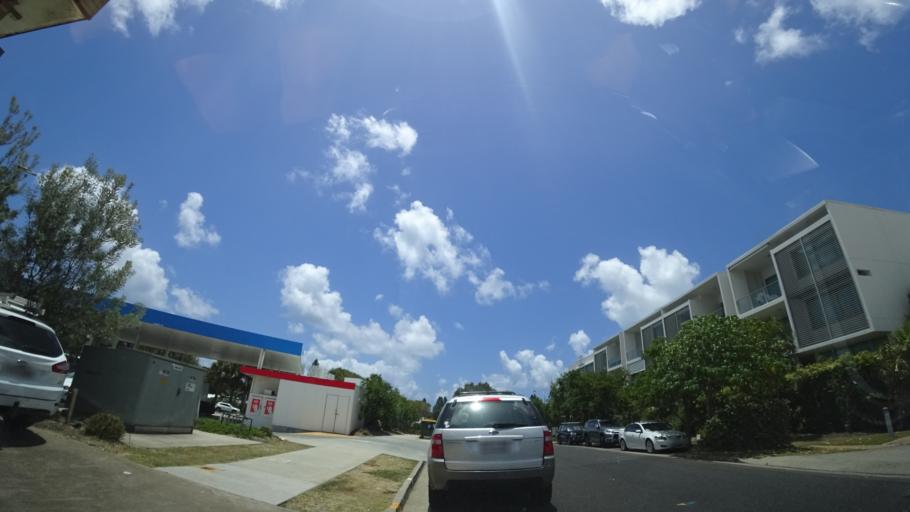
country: AU
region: Queensland
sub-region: Sunshine Coast
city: Coolum Beach
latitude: -26.5280
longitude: 153.0901
